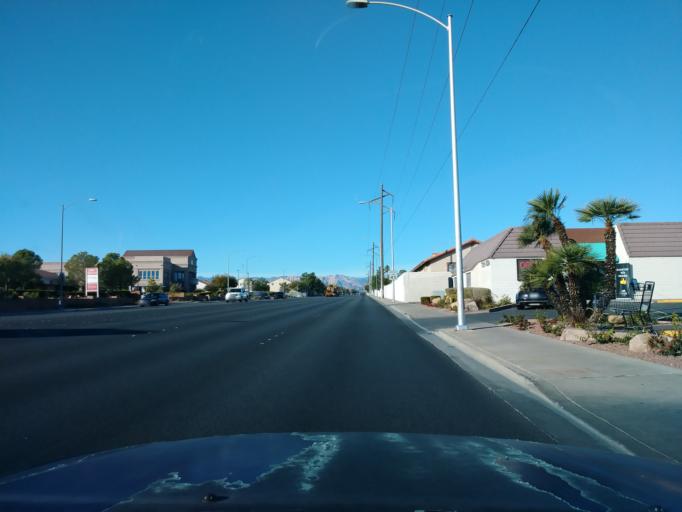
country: US
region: Nevada
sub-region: Clark County
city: Spring Valley
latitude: 36.1592
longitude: -115.2514
